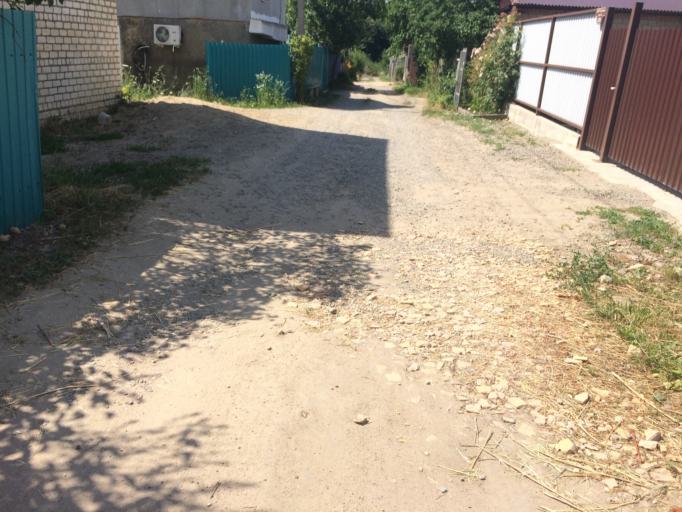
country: RU
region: Stavropol'skiy
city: Tatarka
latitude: 44.9810
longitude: 41.9407
